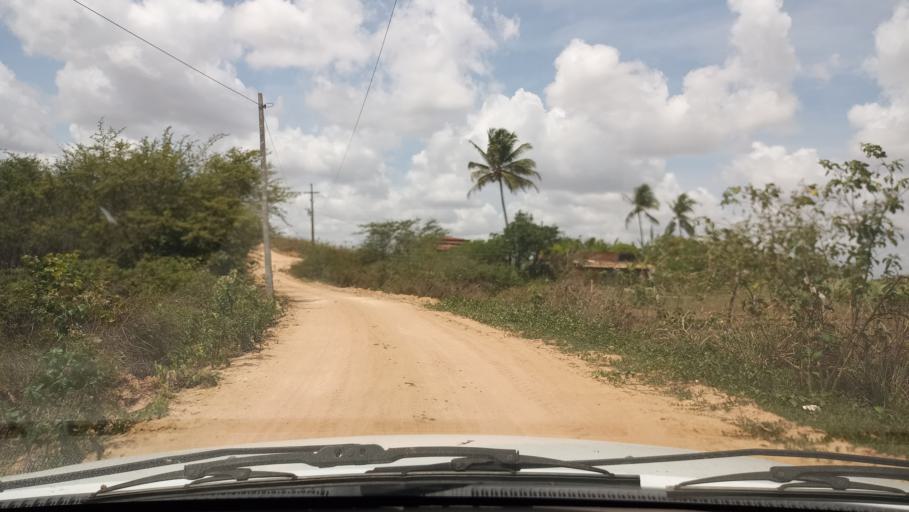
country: BR
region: Rio Grande do Norte
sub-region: Brejinho
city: Brejinho
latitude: -6.2558
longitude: -35.3387
